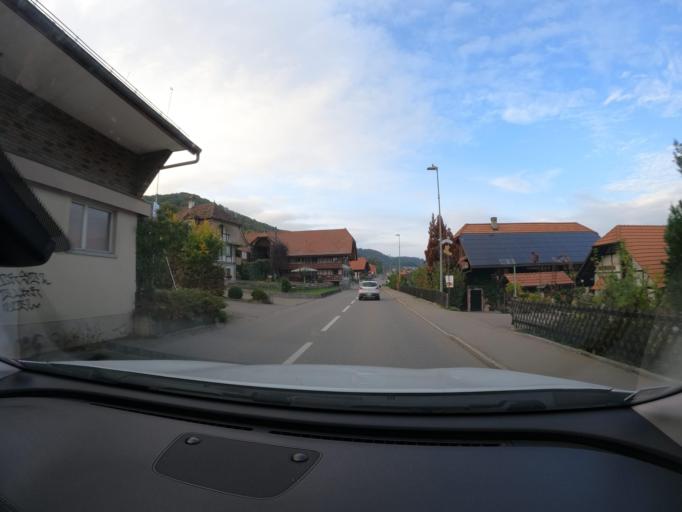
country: CH
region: Bern
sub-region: Bern-Mittelland District
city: Toffen
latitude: 46.8582
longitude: 7.4912
